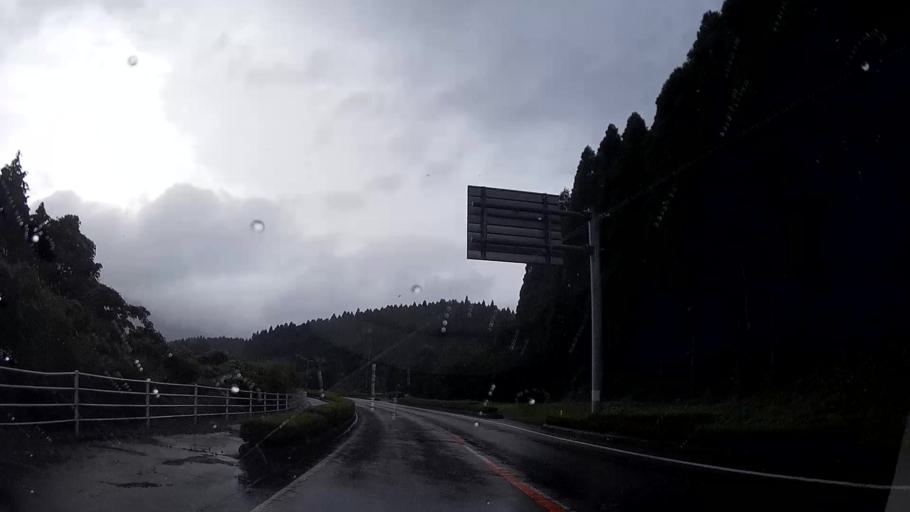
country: JP
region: Kumamoto
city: Aso
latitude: 32.8553
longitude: 131.0176
